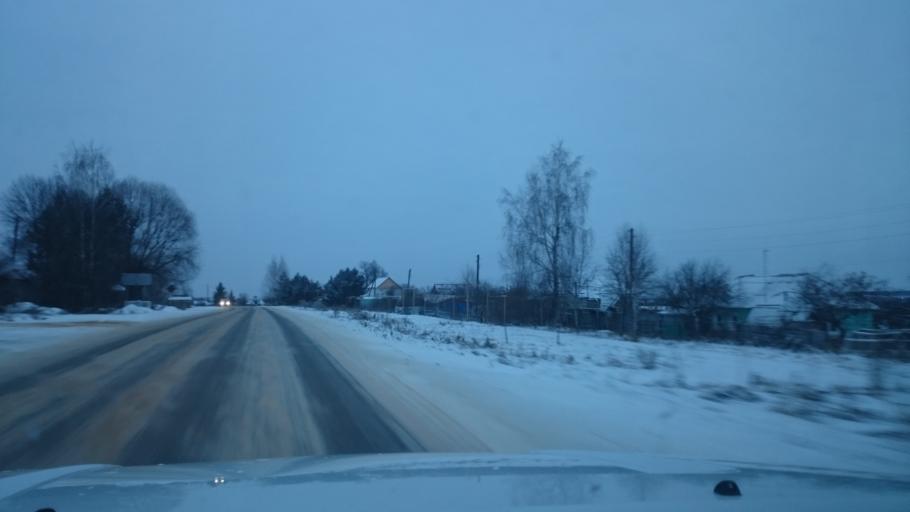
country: RU
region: Tula
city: Leninskiy
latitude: 54.2515
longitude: 37.3755
